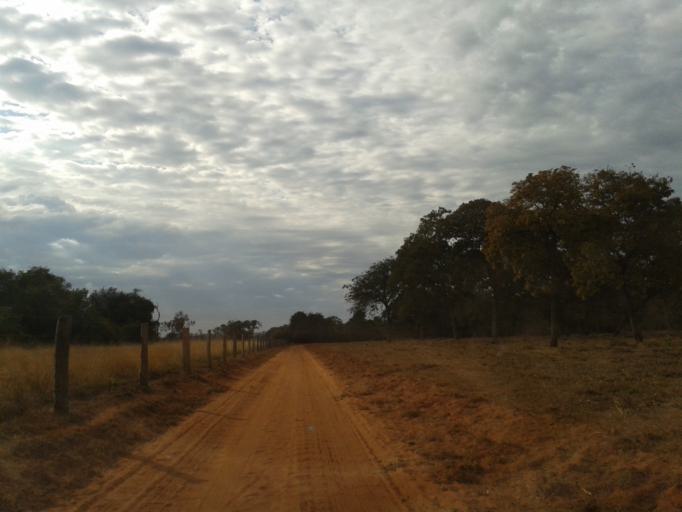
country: BR
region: Minas Gerais
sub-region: Santa Vitoria
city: Santa Vitoria
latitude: -18.7512
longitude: -50.1977
